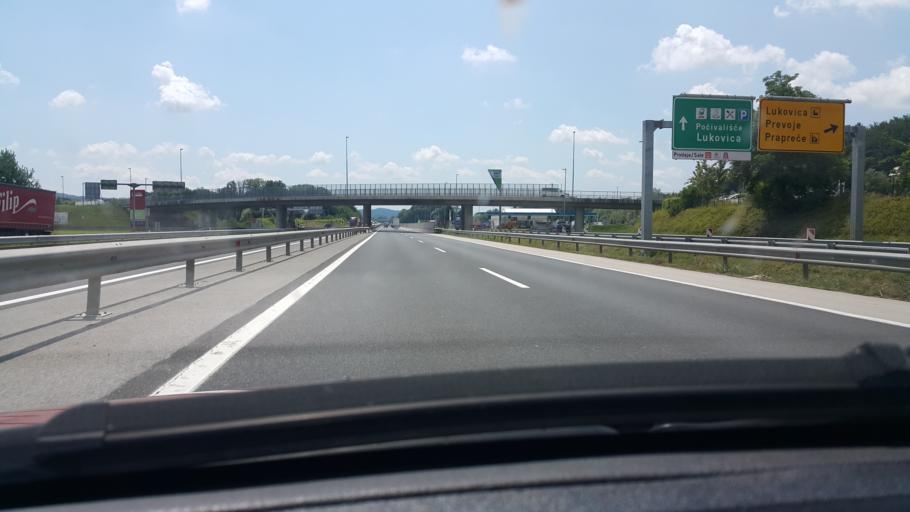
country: SI
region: Lukovica
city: Lukovica pri Domzalah
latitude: 46.1677
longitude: 14.6924
